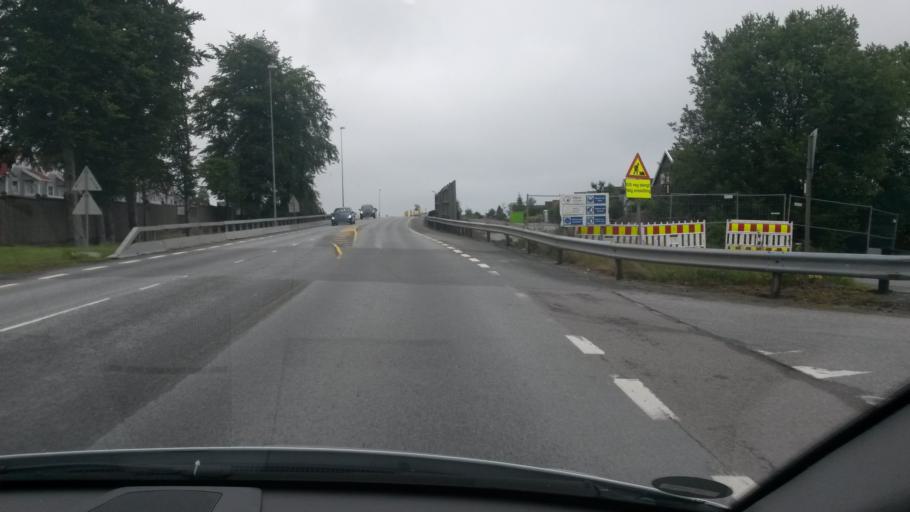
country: NO
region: Rogaland
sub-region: Sandnes
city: Sandnes
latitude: 58.8355
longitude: 5.7214
